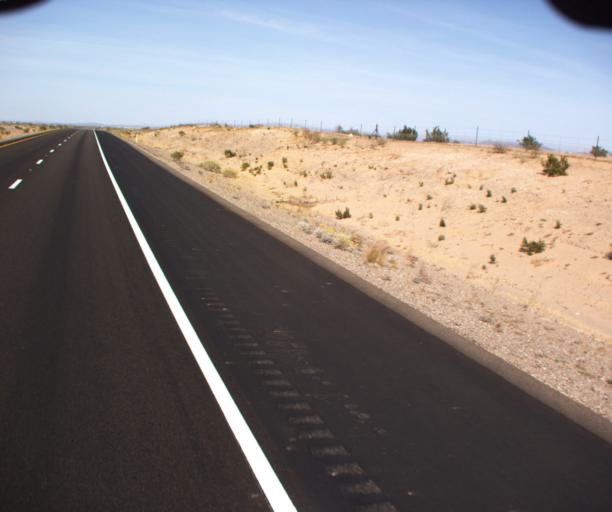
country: US
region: Arizona
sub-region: Yuma County
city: Somerton
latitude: 32.5612
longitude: -114.5608
